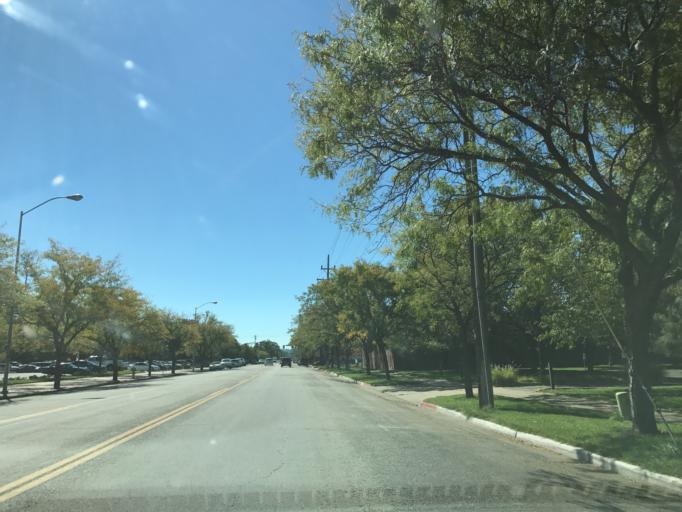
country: US
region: Utah
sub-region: Weber County
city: Ogden
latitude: 41.2225
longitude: -111.9760
